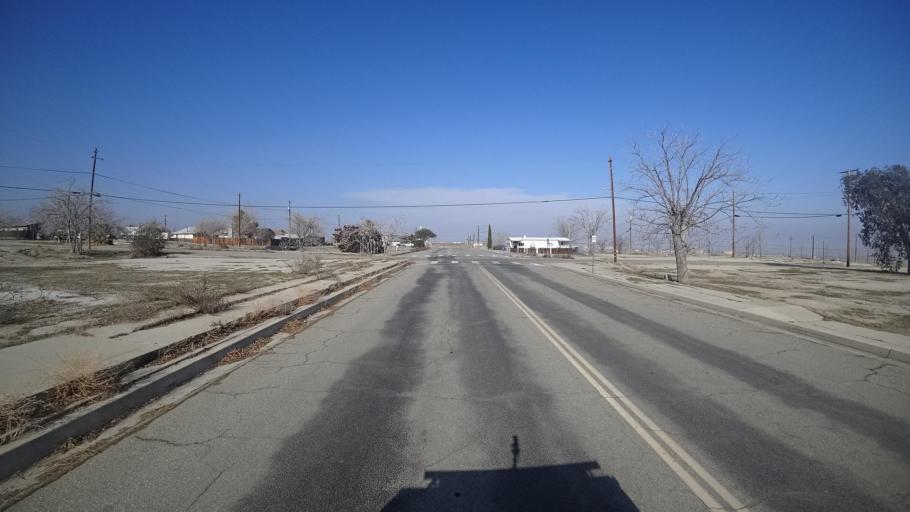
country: US
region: California
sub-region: Kern County
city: Taft Heights
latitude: 35.1782
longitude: -119.5412
